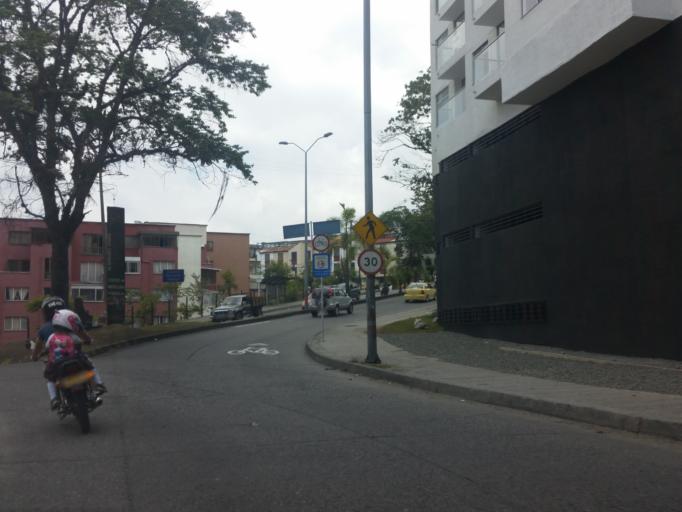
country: CO
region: Caldas
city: Manizales
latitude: 5.0795
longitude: -75.5253
